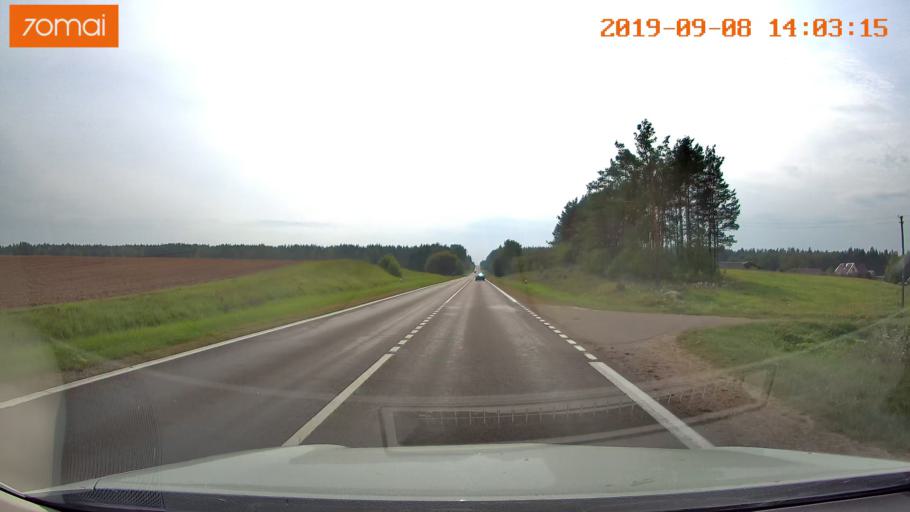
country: LT
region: Alytaus apskritis
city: Druskininkai
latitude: 54.1152
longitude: 24.2070
